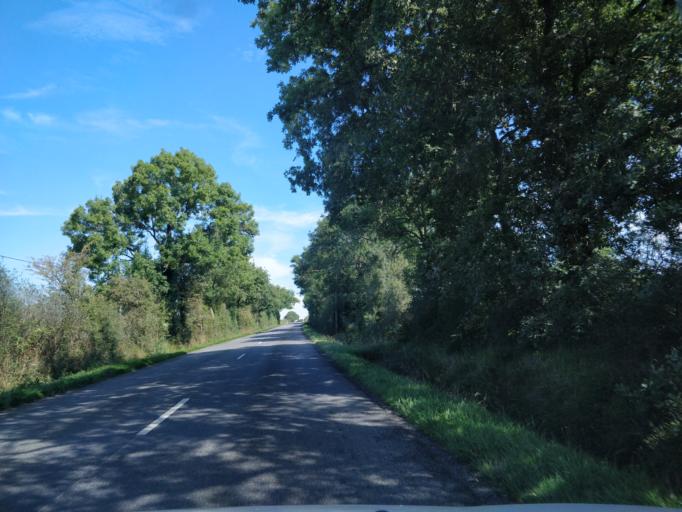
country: FR
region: Pays de la Loire
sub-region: Departement de la Loire-Atlantique
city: Quilly
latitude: 47.4617
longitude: -1.9230
